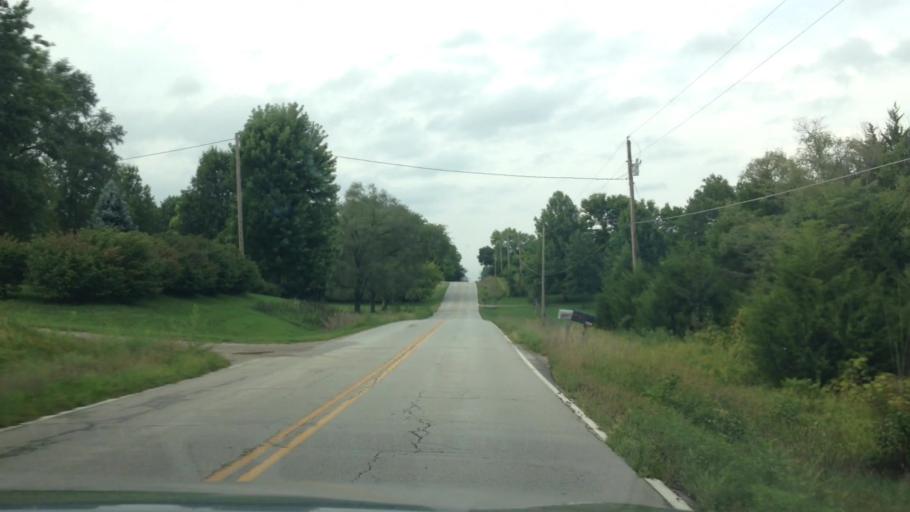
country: US
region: Missouri
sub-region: Clay County
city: Smithville
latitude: 39.3782
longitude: -94.6669
